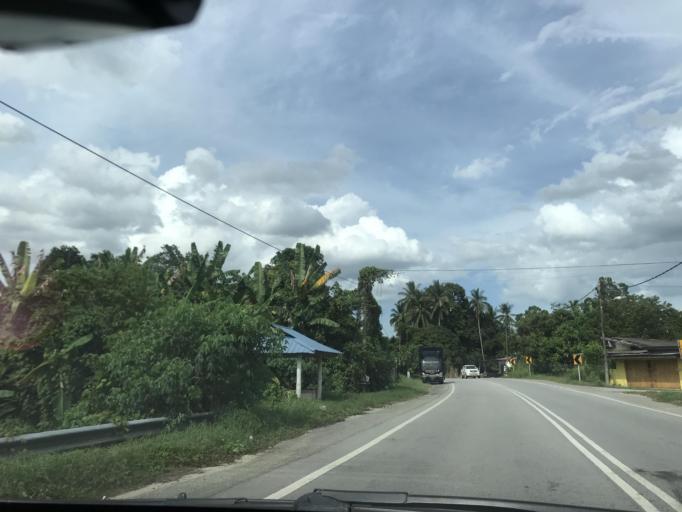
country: MY
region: Kelantan
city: Kampung Lemal
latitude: 6.0331
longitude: 102.1644
